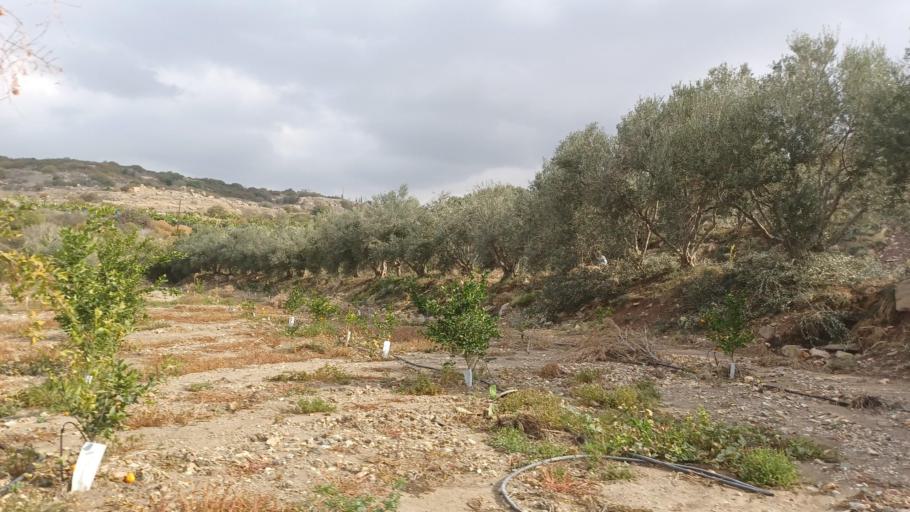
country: CY
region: Pafos
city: Kissonerga
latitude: 34.8440
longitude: 32.3941
